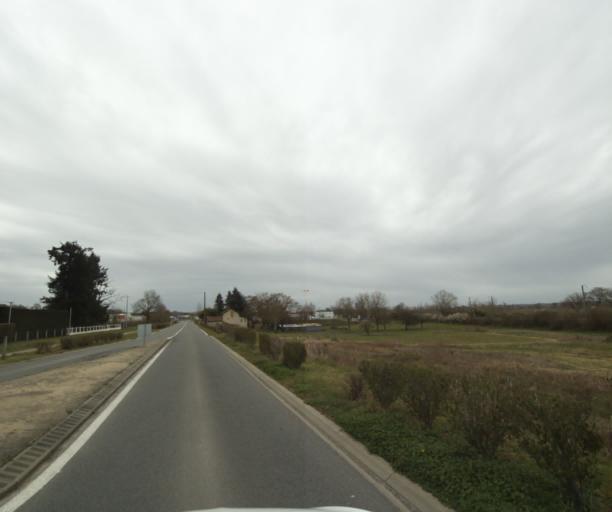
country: FR
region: Auvergne
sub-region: Departement de l'Allier
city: Toulon-sur-Allier
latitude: 46.5102
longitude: 3.3607
